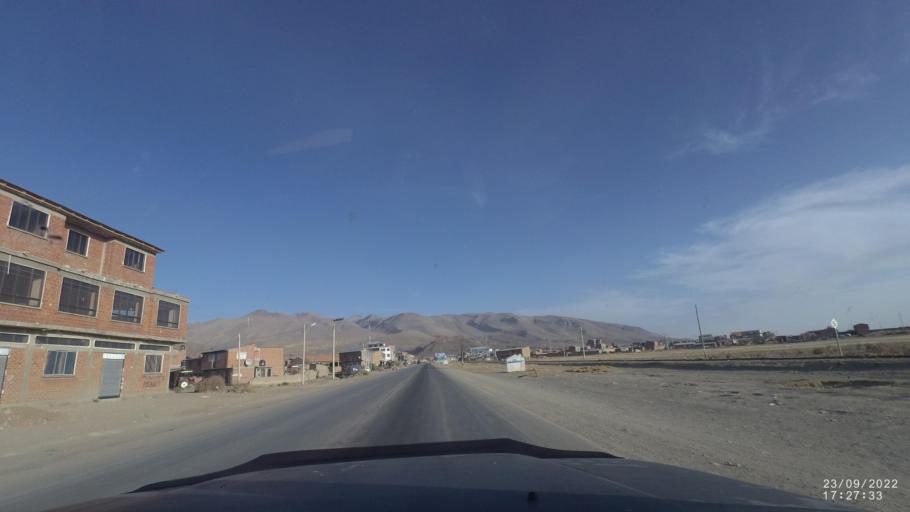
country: BO
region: Oruro
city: Challapata
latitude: -18.8909
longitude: -66.7809
